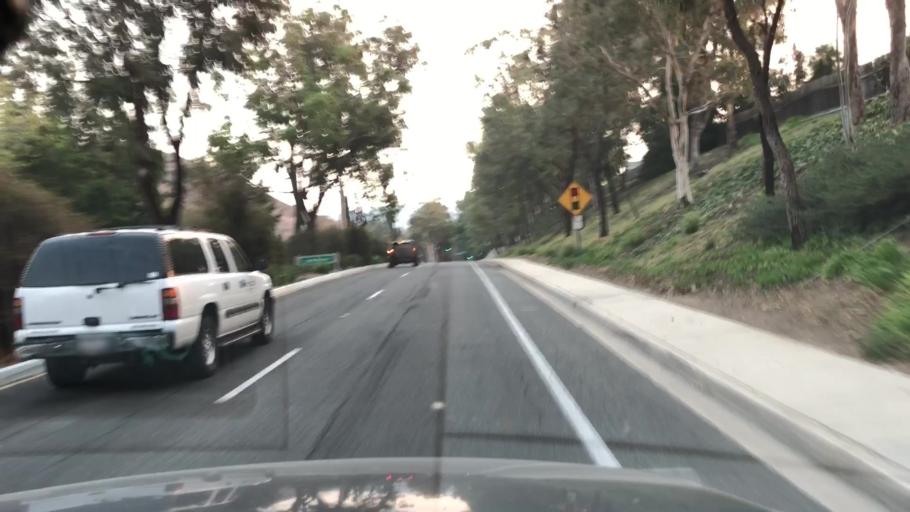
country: US
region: California
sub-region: Ventura County
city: Casa Conejo
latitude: 34.2015
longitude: -118.8903
